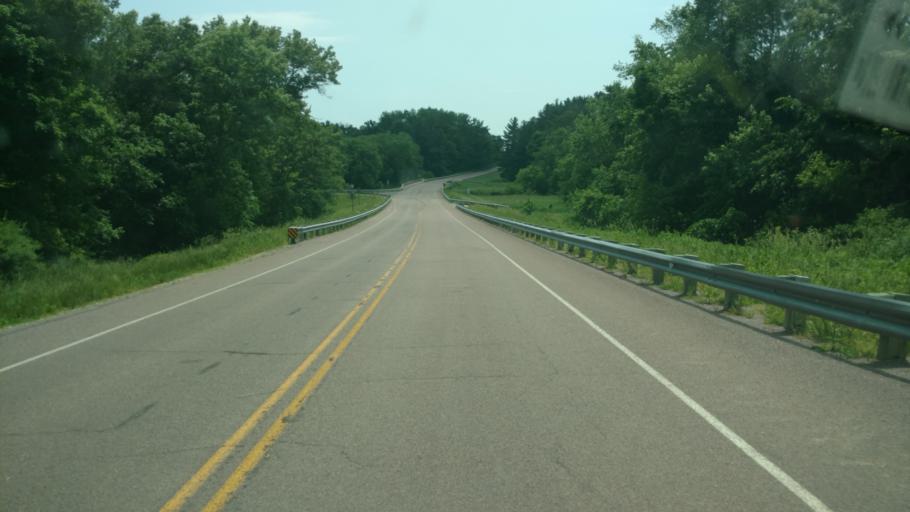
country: US
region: Wisconsin
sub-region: Monroe County
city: Cashton
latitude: 43.6534
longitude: -90.5942
